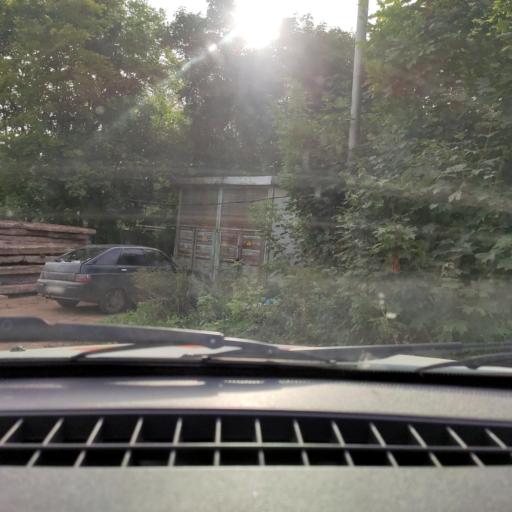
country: RU
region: Bashkortostan
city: Ufa
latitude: 54.7240
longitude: 56.0231
